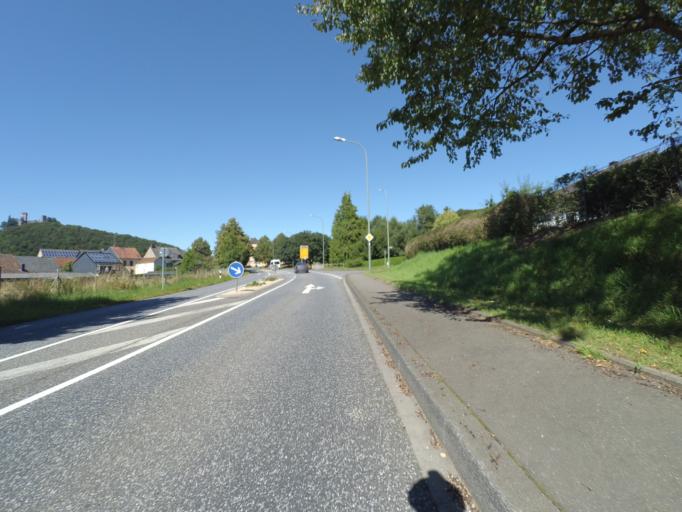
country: DE
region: Rheinland-Pfalz
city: Pelm
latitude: 50.2326
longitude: 6.6908
